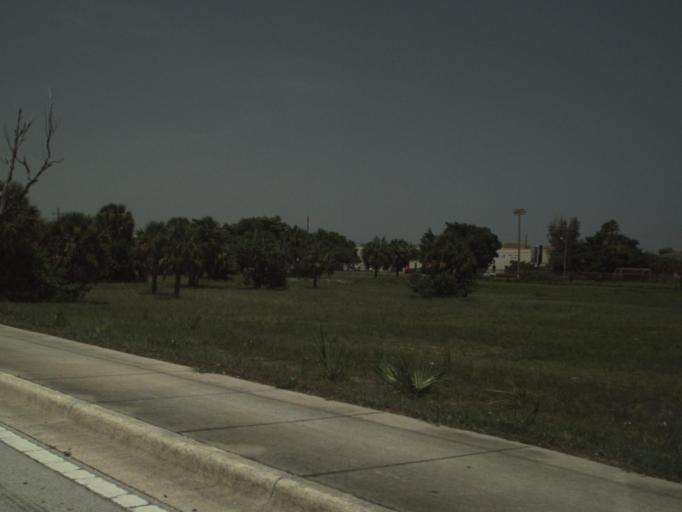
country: US
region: Florida
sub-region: Broward County
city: Pompano Beach
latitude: 26.2410
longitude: -80.1514
